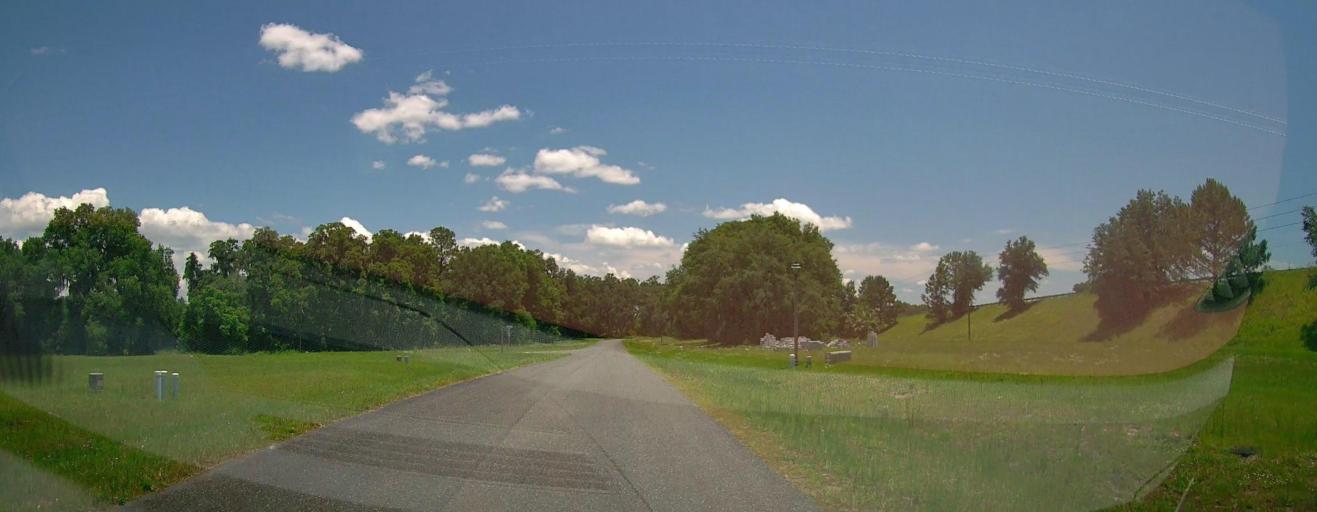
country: US
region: Florida
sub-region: Marion County
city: Belleview
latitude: 29.0893
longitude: -82.0756
